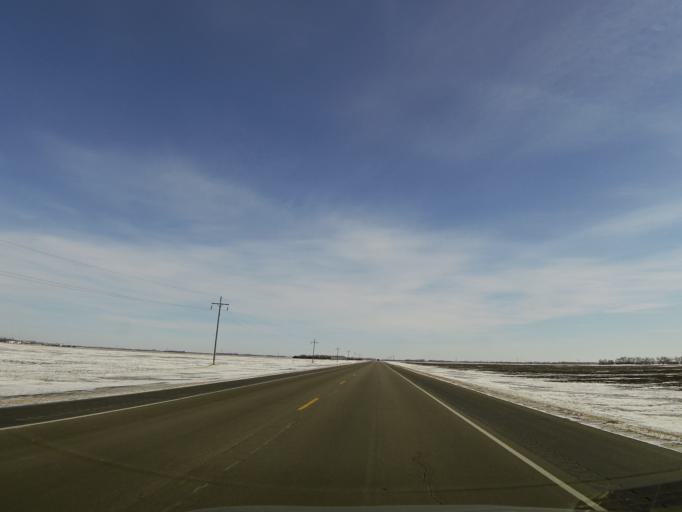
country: US
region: North Dakota
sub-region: Walsh County
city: Grafton
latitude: 48.4123
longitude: -97.2911
